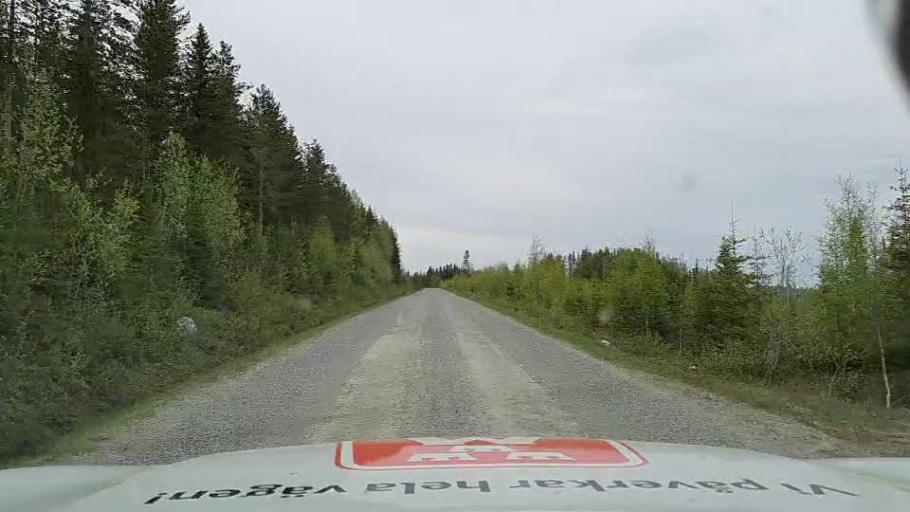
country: SE
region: Jaemtland
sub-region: OEstersunds Kommun
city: Brunflo
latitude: 62.6290
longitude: 14.9414
